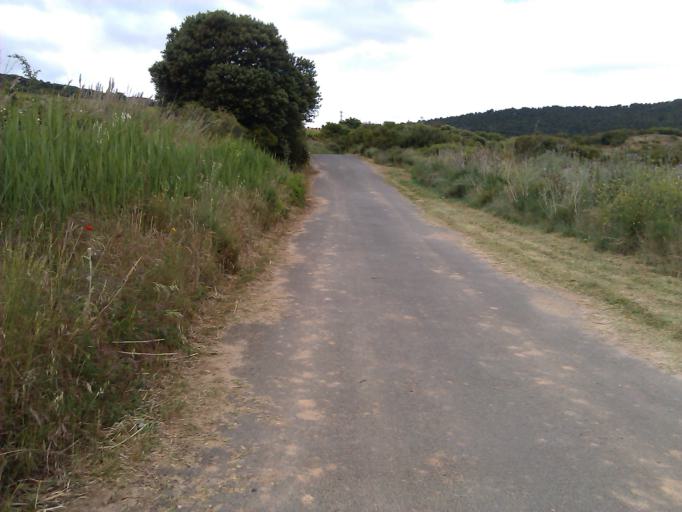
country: ES
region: La Rioja
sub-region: Provincia de La Rioja
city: Navarrete
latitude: 42.4377
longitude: -2.5181
